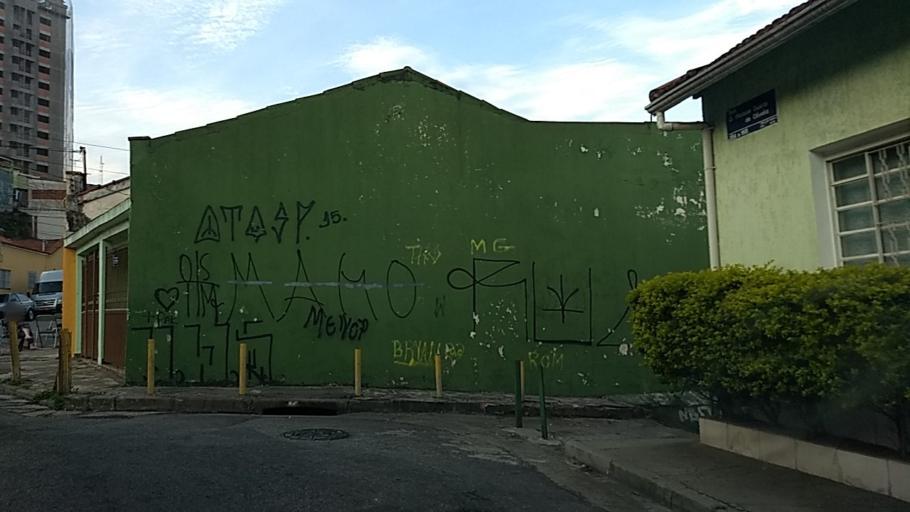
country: BR
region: Sao Paulo
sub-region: Sao Paulo
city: Sao Paulo
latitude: -23.5140
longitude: -46.5805
